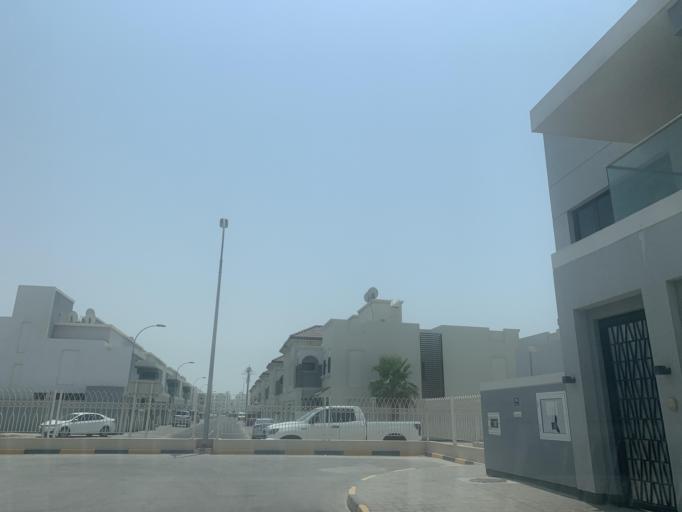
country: BH
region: Muharraq
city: Al Muharraq
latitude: 26.3112
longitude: 50.6261
